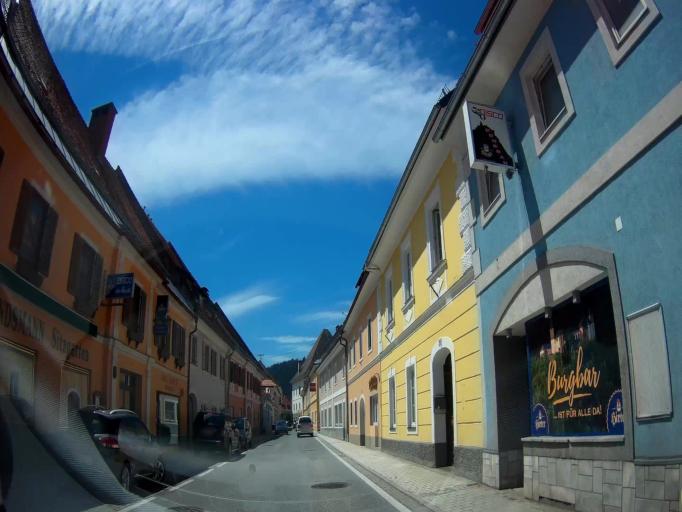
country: AT
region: Carinthia
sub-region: Politischer Bezirk Sankt Veit an der Glan
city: Strassburg
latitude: 46.8950
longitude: 14.3309
